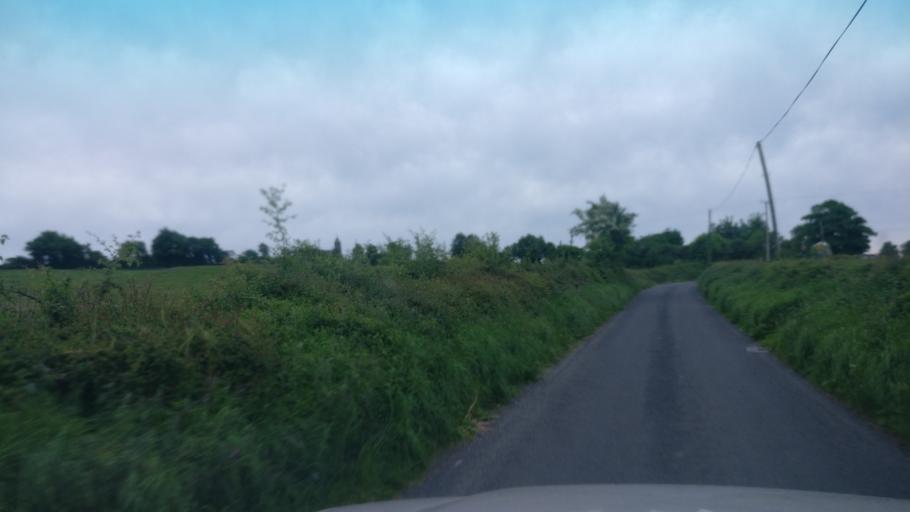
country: IE
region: Connaught
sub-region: County Galway
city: Portumna
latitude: 53.1153
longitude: -8.2882
